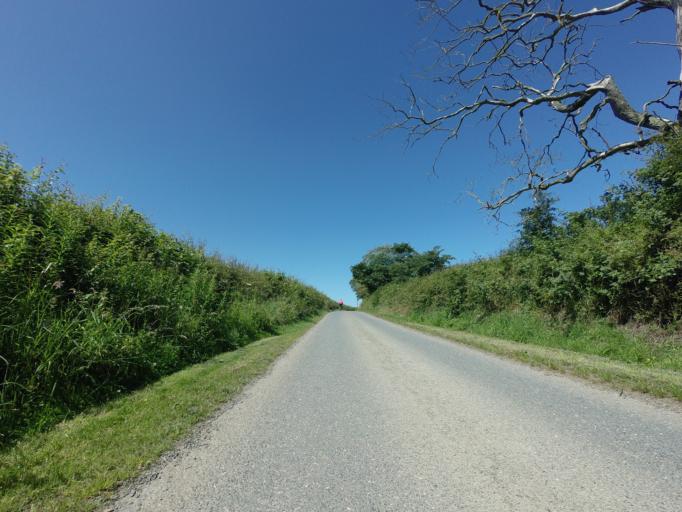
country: GB
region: Scotland
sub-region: Aberdeenshire
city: Macduff
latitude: 57.6332
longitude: -2.4888
